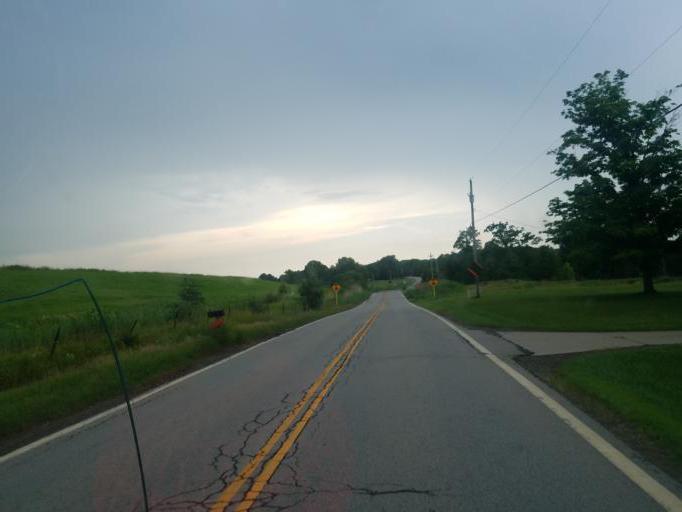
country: US
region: Ohio
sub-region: Wayne County
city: Rittman
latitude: 40.9457
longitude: -81.7600
